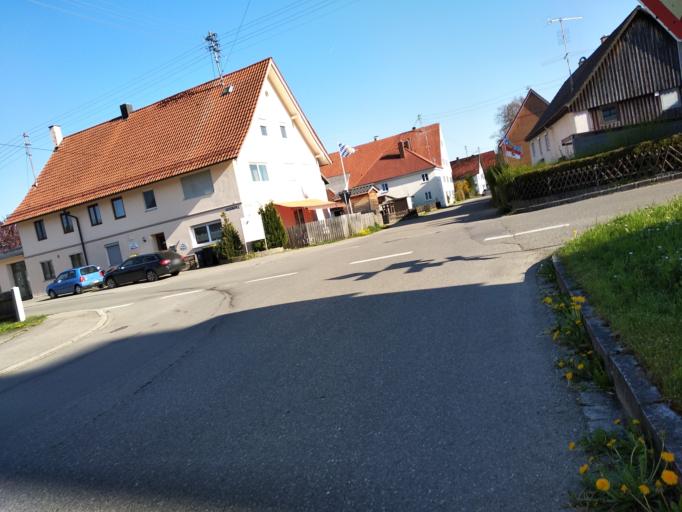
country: DE
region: Bavaria
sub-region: Swabia
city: Erkheim
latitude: 48.0377
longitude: 10.3394
